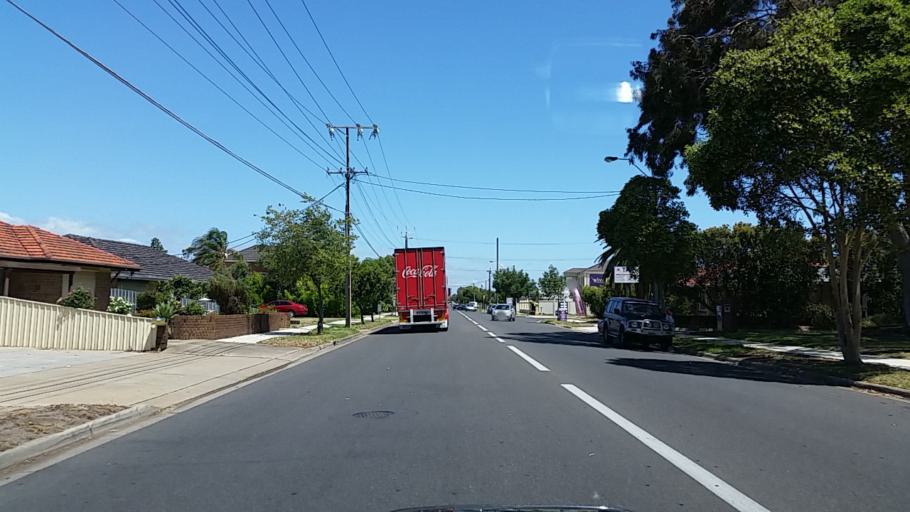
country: AU
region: South Australia
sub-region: Charles Sturt
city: Findon
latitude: -34.9102
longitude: 138.5335
